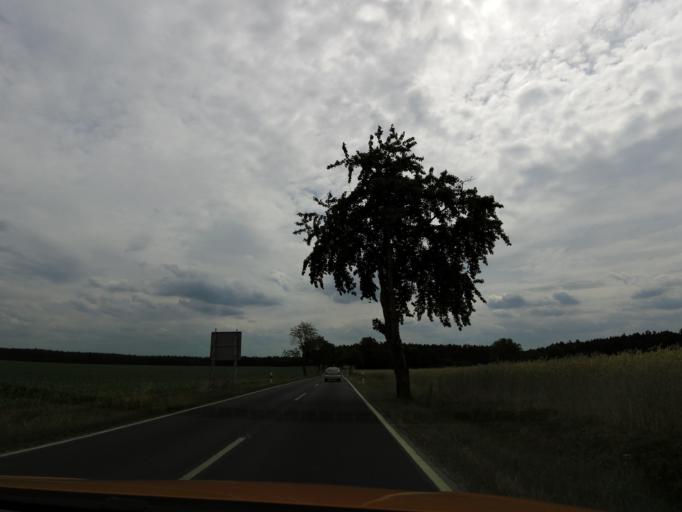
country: DE
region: Brandenburg
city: Rangsdorf
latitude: 52.2414
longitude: 13.3883
